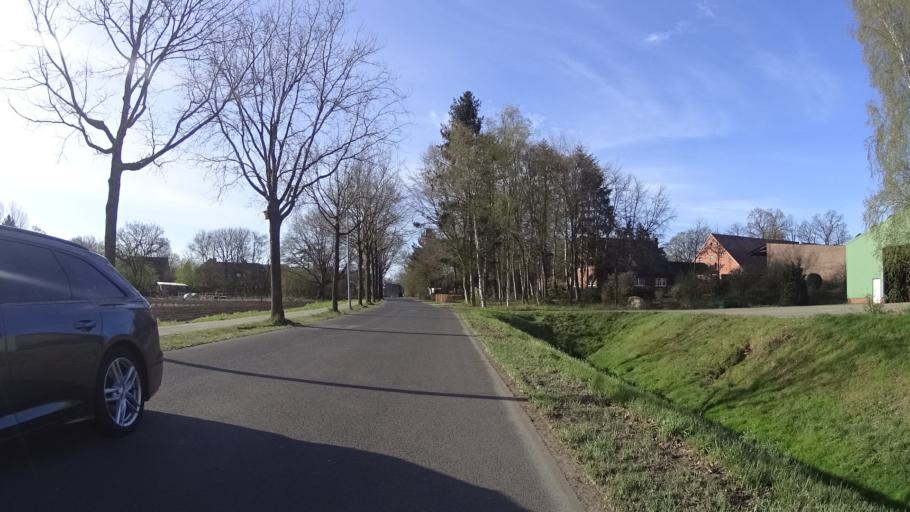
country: DE
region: Lower Saxony
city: Haren
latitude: 52.7891
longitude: 7.2788
